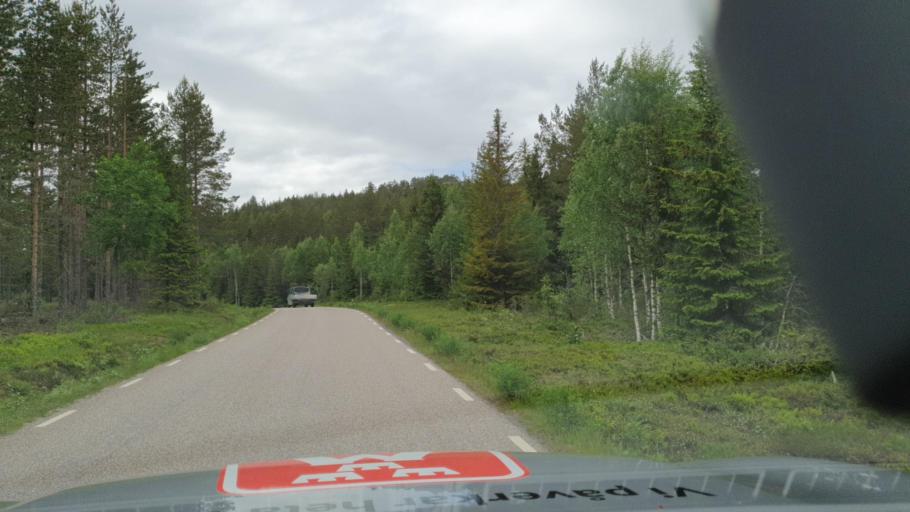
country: SE
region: Vaesternorrland
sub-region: Kramfors Kommun
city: Nordingra
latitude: 62.8620
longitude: 18.3439
